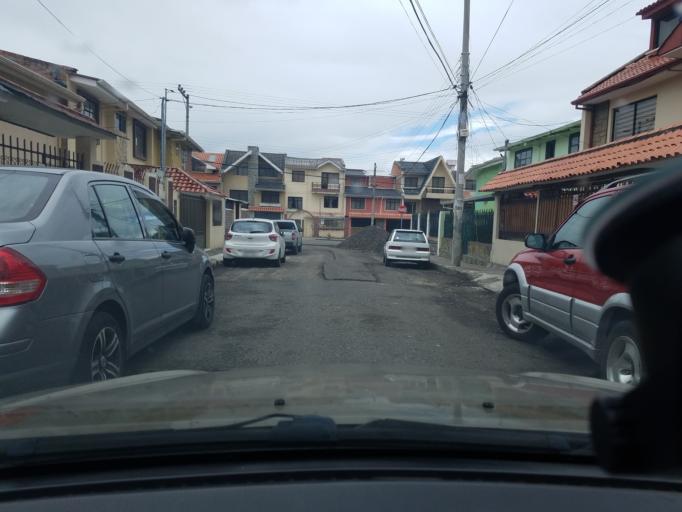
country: EC
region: Azuay
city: Cuenca
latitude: -2.9038
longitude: -78.9880
